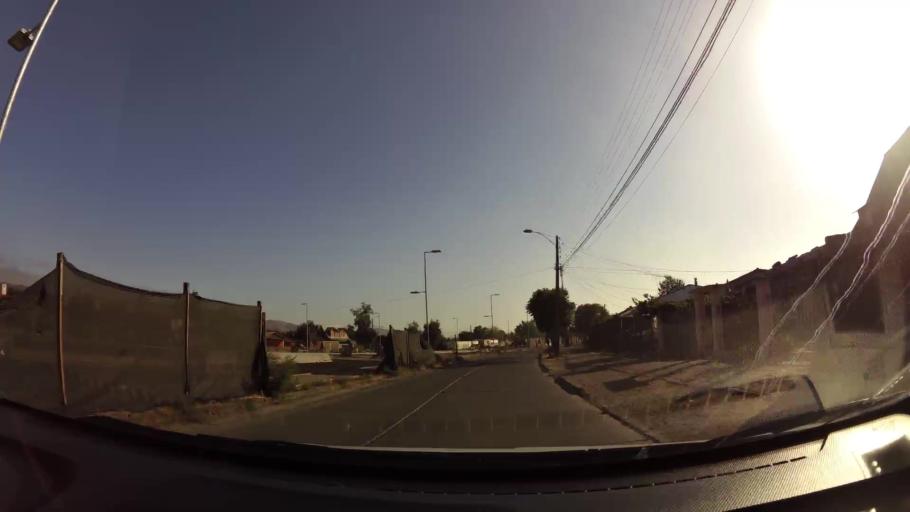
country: CL
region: Maule
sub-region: Provincia de Talca
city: Talca
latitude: -35.4085
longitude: -71.6591
